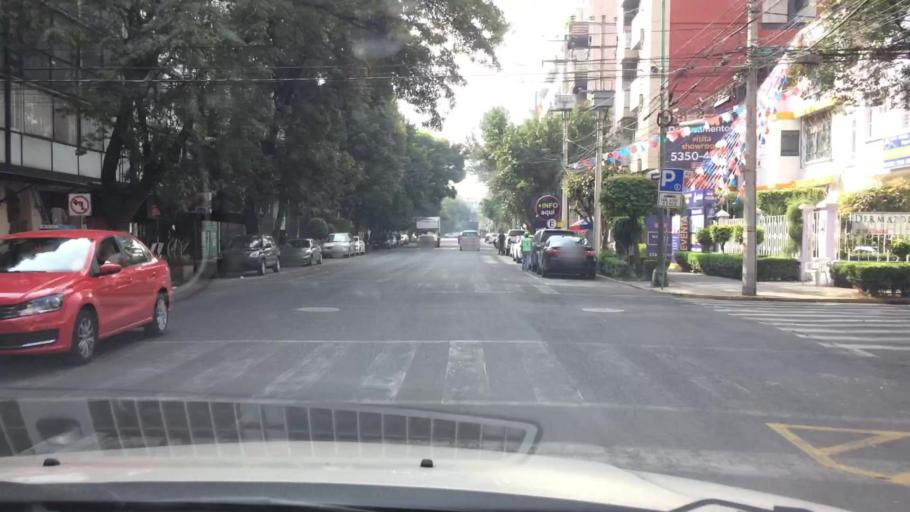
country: MX
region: Mexico City
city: Colonia del Valle
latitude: 19.3879
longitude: -99.1776
